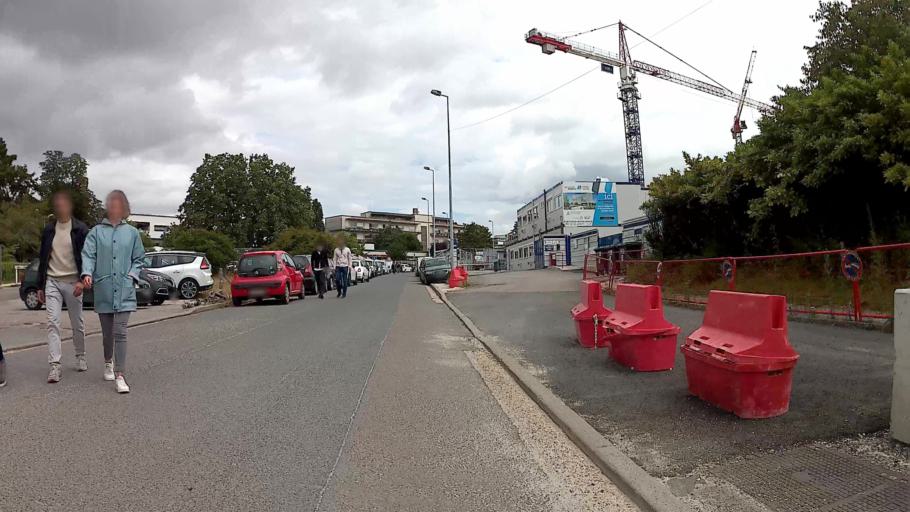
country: FR
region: Aquitaine
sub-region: Departement de la Gironde
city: Merignac
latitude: 44.8254
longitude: -0.6097
